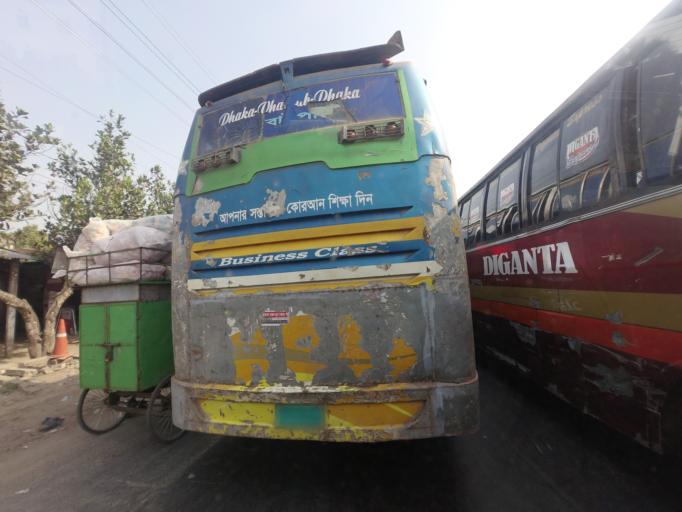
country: BD
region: Dhaka
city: Narsingdi
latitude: 23.8471
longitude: 90.6293
